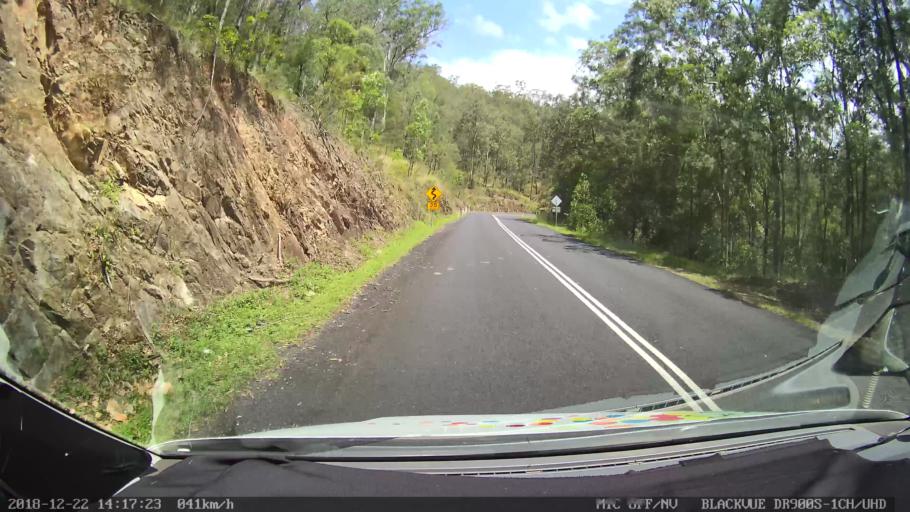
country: AU
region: New South Wales
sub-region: Clarence Valley
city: Coutts Crossing
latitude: -30.0080
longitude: 152.6680
